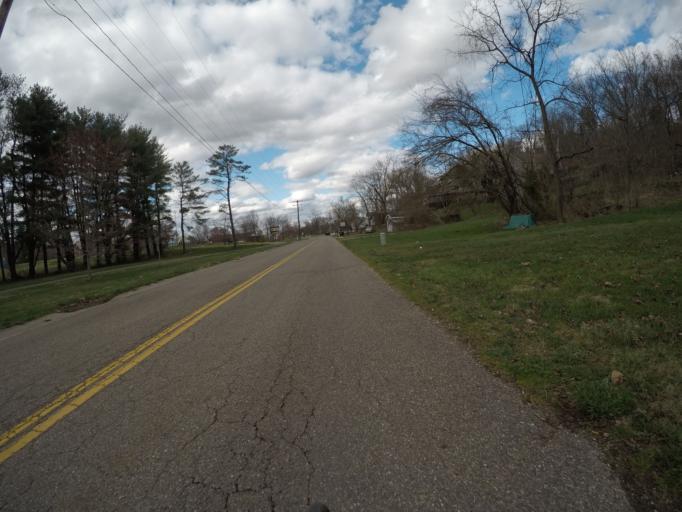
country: US
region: Ohio
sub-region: Washington County
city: Marietta
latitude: 39.4334
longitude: -81.4665
